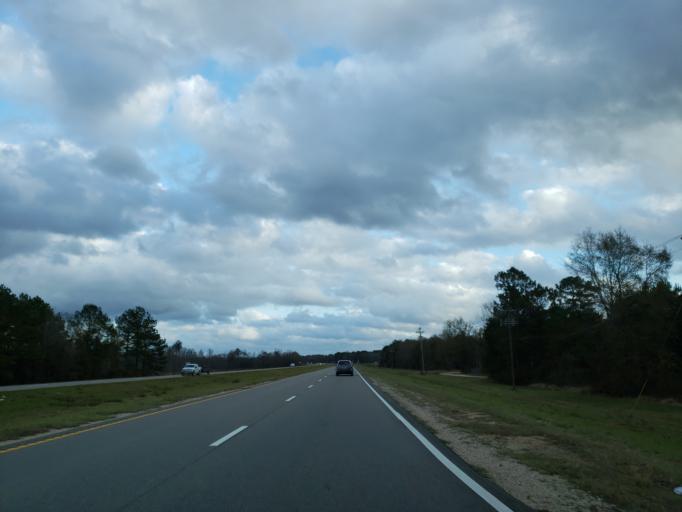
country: US
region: Mississippi
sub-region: Perry County
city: New Augusta
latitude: 31.1132
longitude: -88.8204
